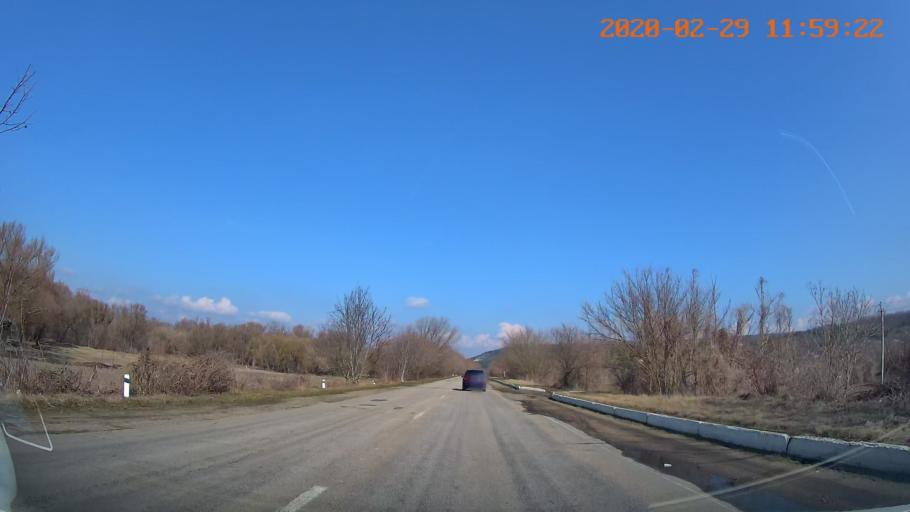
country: MD
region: Telenesti
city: Ribnita
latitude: 47.8243
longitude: 29.0166
